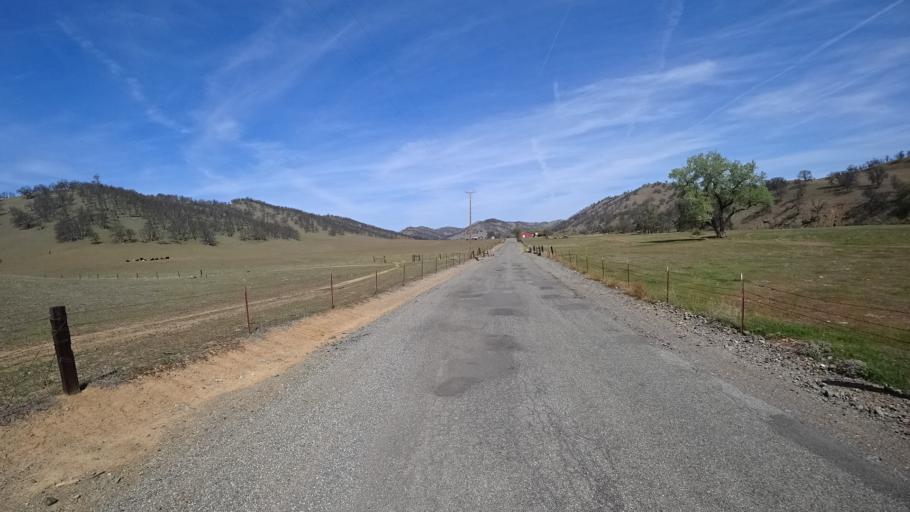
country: US
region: California
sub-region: Glenn County
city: Willows
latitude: 39.5150
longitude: -122.4565
